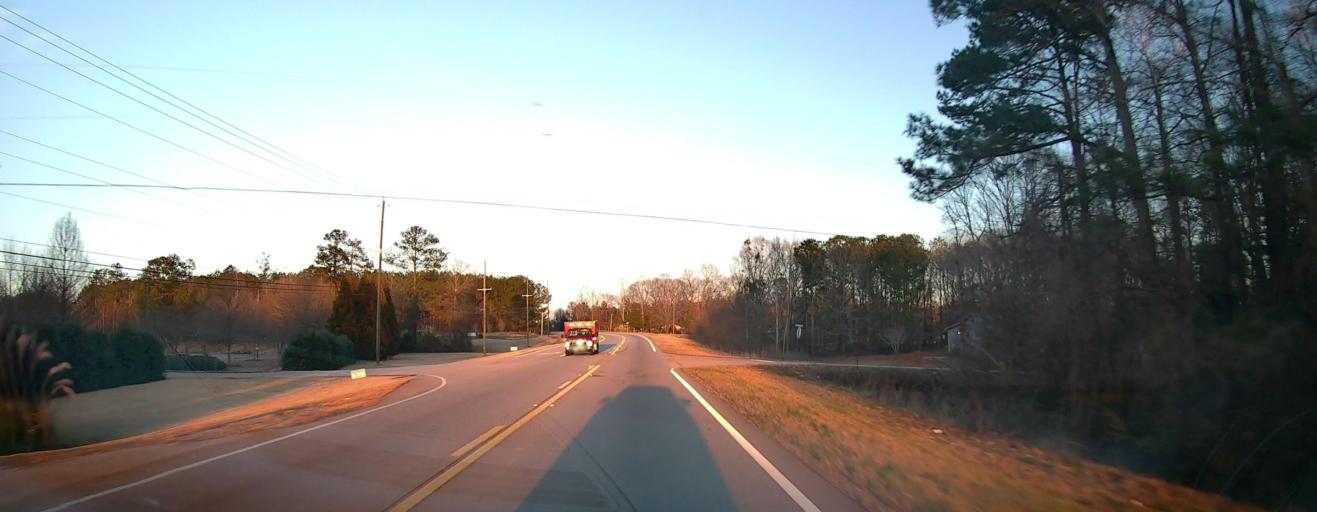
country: US
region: Georgia
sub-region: Troup County
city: La Grange
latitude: 33.0173
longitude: -85.0000
